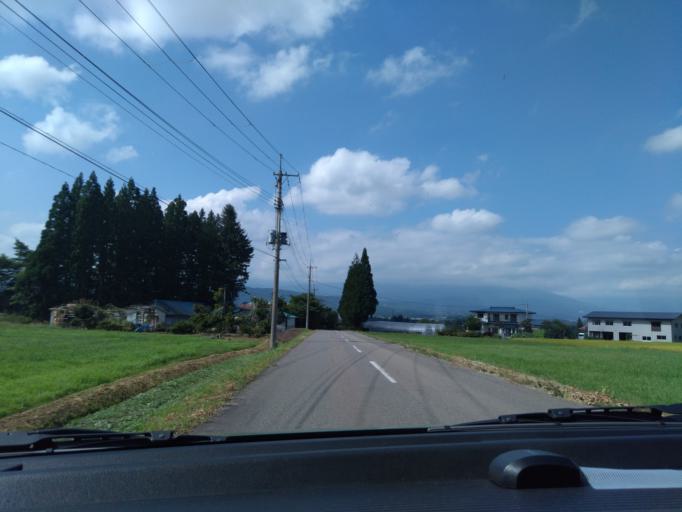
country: JP
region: Iwate
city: Shizukuishi
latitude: 39.6781
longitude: 140.9605
